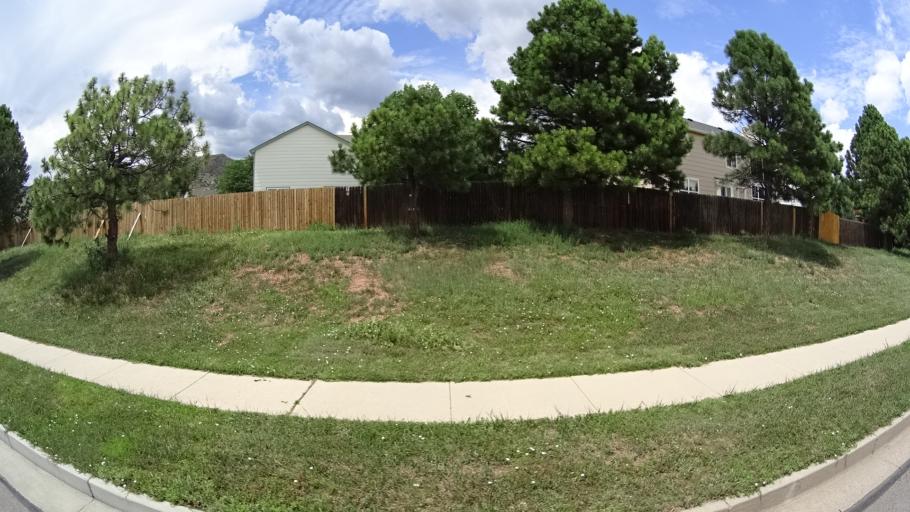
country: US
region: Colorado
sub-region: El Paso County
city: Manitou Springs
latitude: 38.9016
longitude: -104.8682
